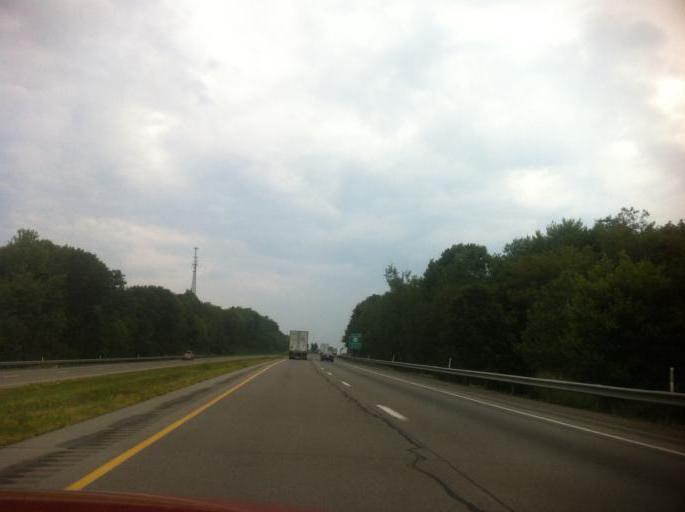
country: US
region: Pennsylvania
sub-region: Jefferson County
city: Brookville
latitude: 41.1832
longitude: -79.1567
